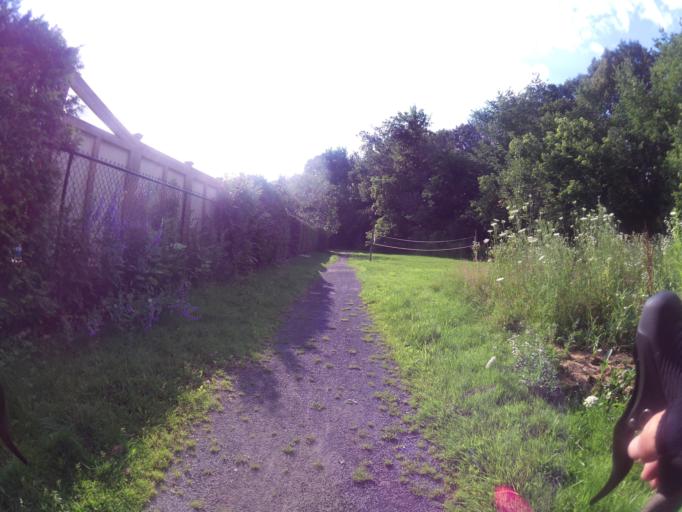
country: CA
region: Ontario
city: Ottawa
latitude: 45.2886
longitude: -75.6846
